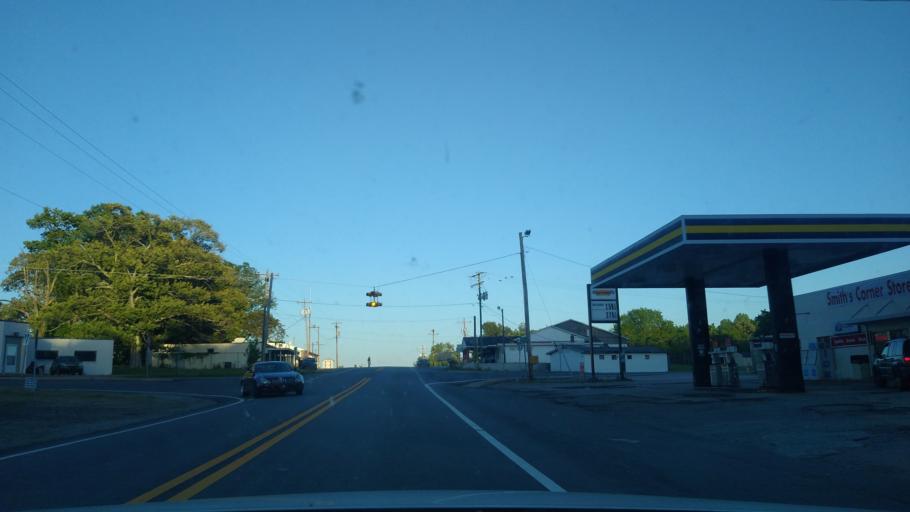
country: US
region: North Carolina
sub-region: Rockingham County
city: Reidsville
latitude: 36.3897
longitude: -79.5054
